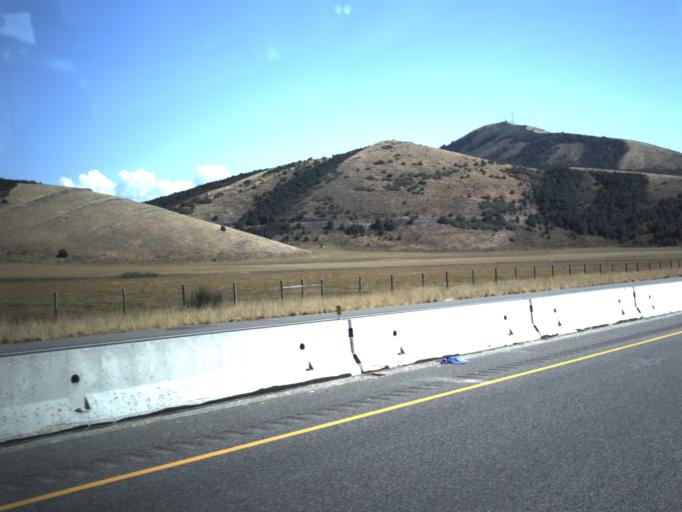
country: US
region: Utah
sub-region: Box Elder County
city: Brigham City
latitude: 41.5681
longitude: -111.9668
